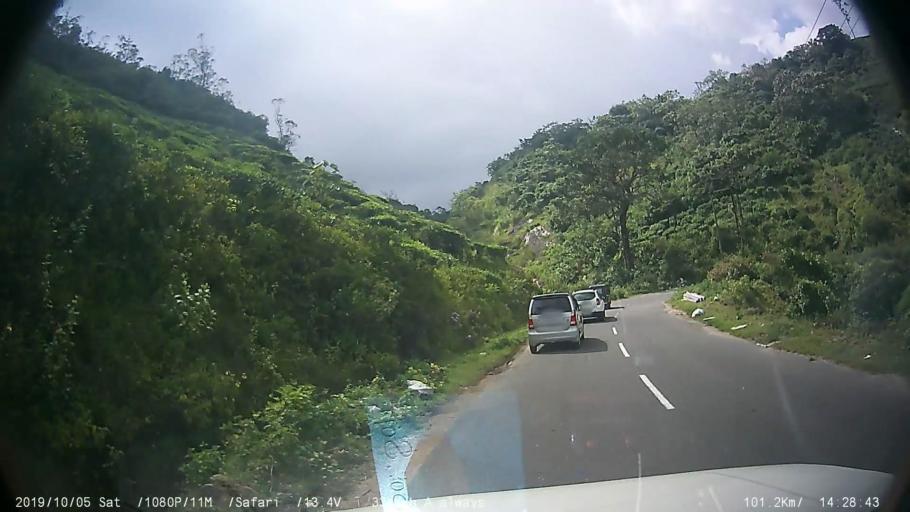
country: IN
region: Kerala
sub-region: Kottayam
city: Erattupetta
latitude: 9.6080
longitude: 76.9662
